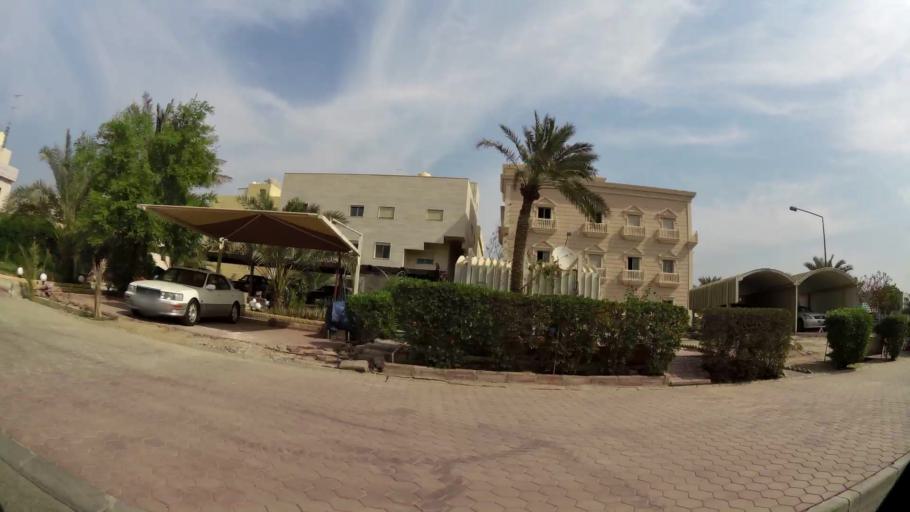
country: KW
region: Al Asimah
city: Ash Shamiyah
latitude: 29.3409
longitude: 47.9761
